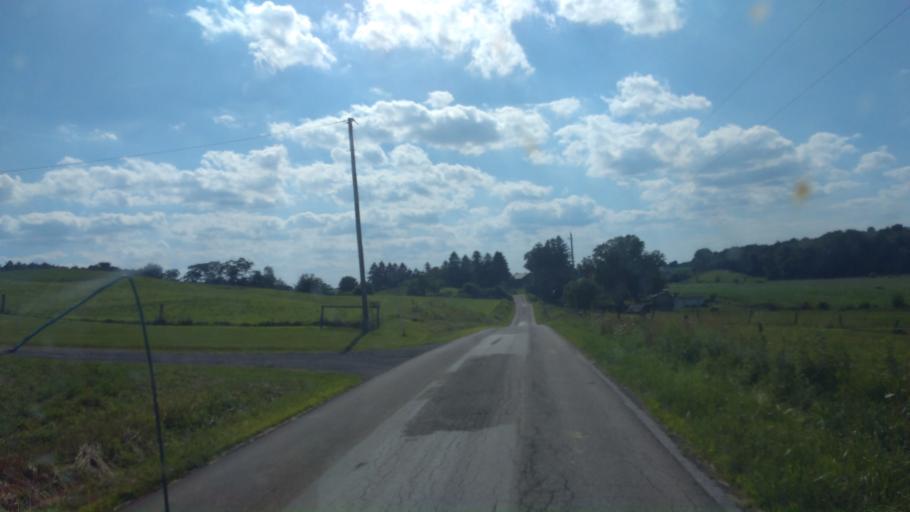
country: US
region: Ohio
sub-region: Wayne County
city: Dalton
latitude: 40.7537
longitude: -81.6814
